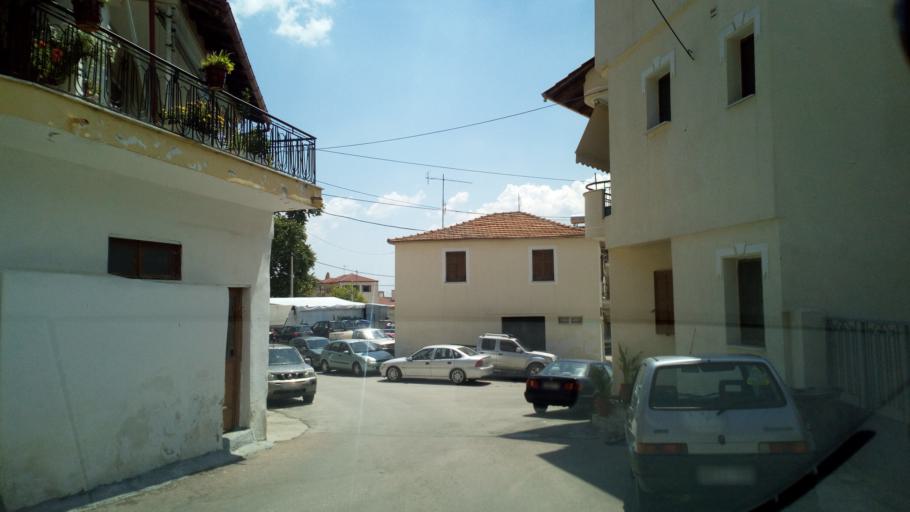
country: GR
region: Central Macedonia
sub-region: Nomos Thessalonikis
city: Sochos
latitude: 40.8190
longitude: 23.3542
